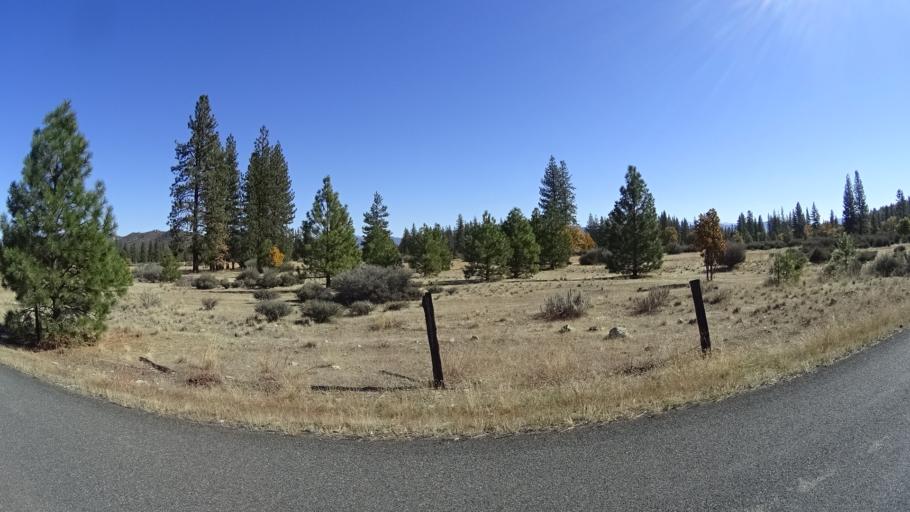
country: US
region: California
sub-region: Siskiyou County
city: Yreka
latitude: 41.5441
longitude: -122.9356
